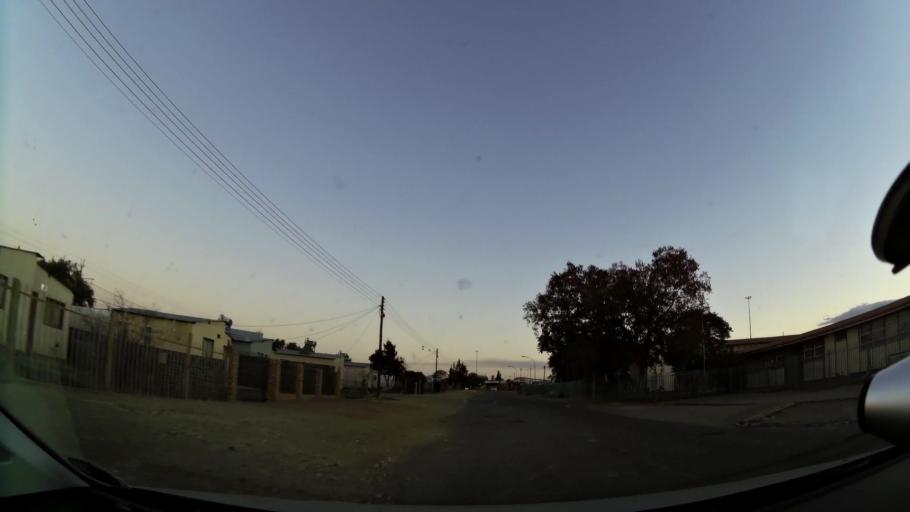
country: ZA
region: Northern Cape
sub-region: Frances Baard District Municipality
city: Kimberley
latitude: -28.7163
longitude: 24.7675
